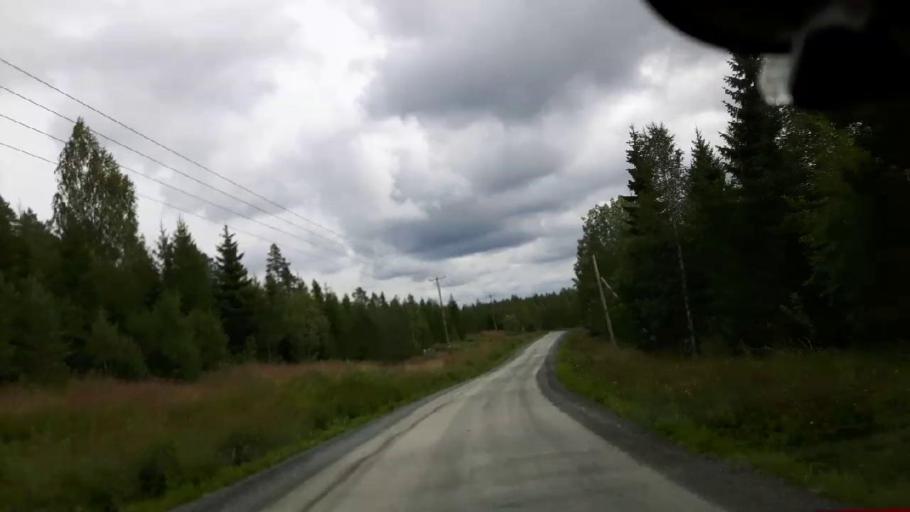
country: SE
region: Jaemtland
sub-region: Krokoms Kommun
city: Krokom
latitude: 63.5825
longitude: 14.1832
